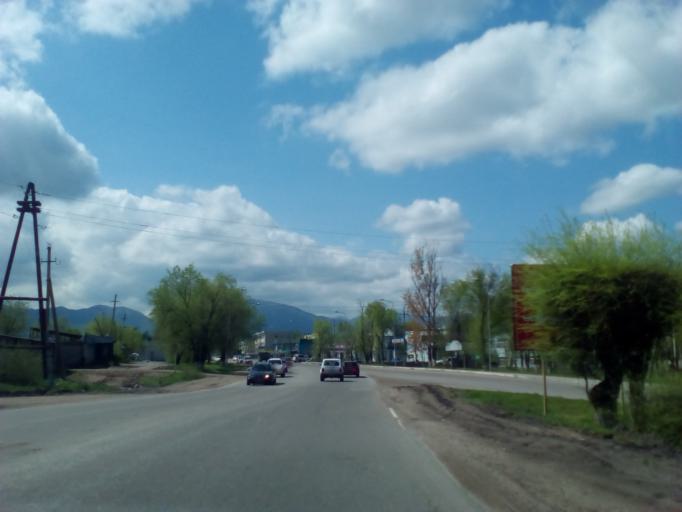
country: KZ
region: Almaty Oblysy
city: Burunday
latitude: 43.2156
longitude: 76.6459
